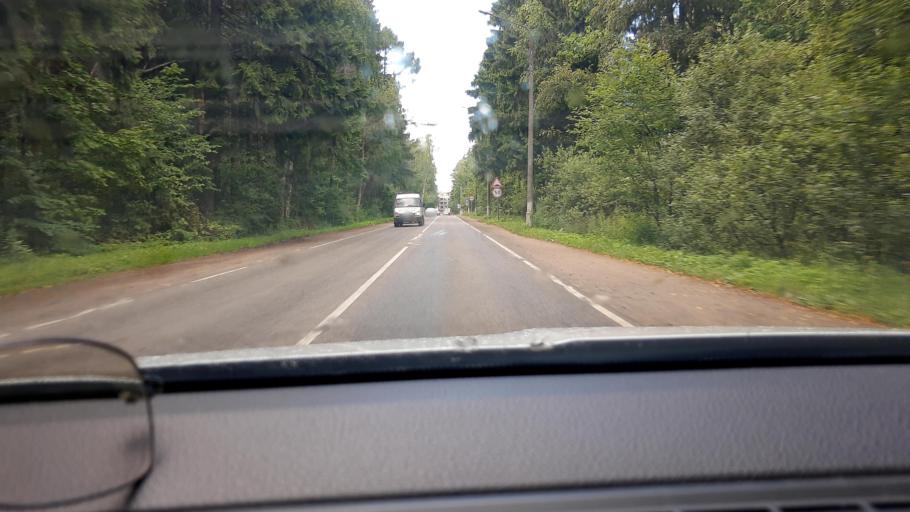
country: RU
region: Moskovskaya
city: Povedniki
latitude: 55.9712
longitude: 37.6111
